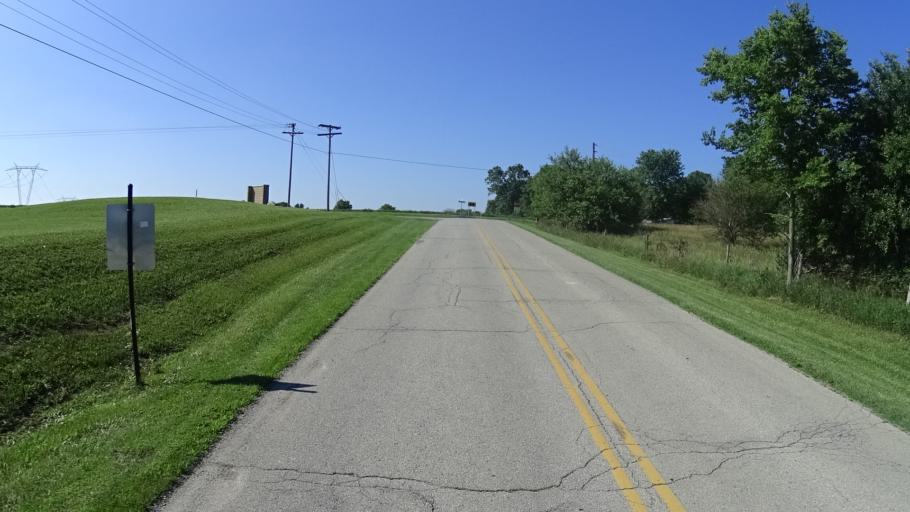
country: US
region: Indiana
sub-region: Madison County
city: Ingalls
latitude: 39.9646
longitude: -85.7962
